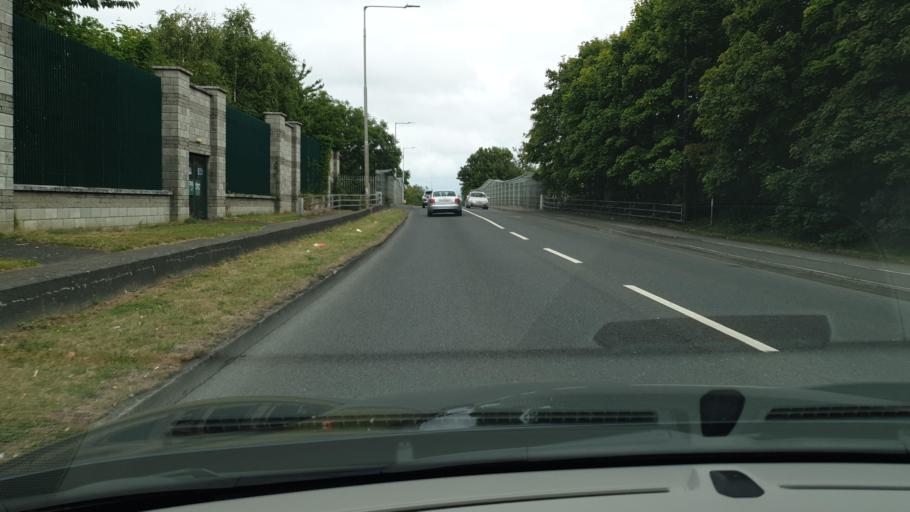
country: IE
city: Palmerstown
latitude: 53.3475
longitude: -6.3876
